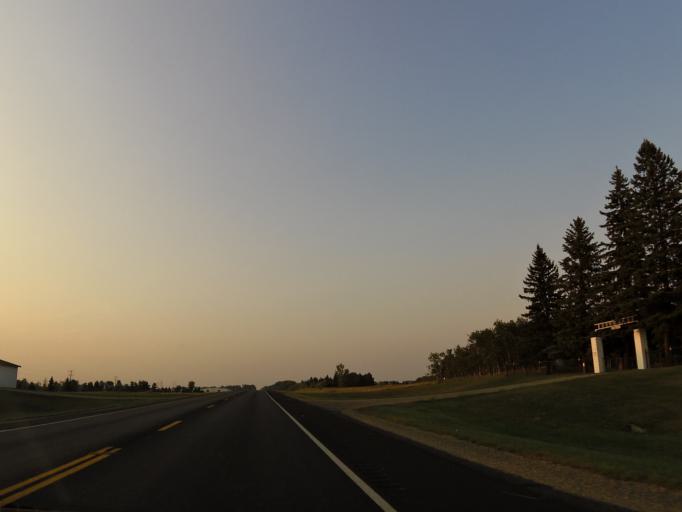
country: US
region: North Dakota
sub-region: Grand Forks County
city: Larimore
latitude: 47.9334
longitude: -97.6240
